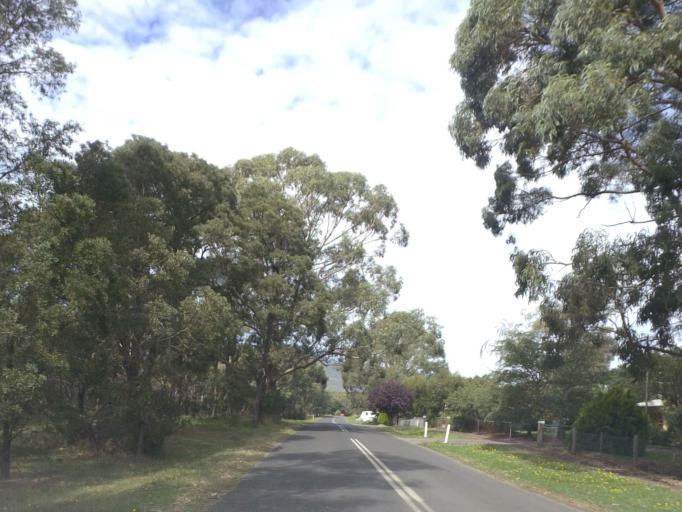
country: AU
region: Victoria
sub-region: Hume
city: Sunbury
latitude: -37.3672
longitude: 144.5394
